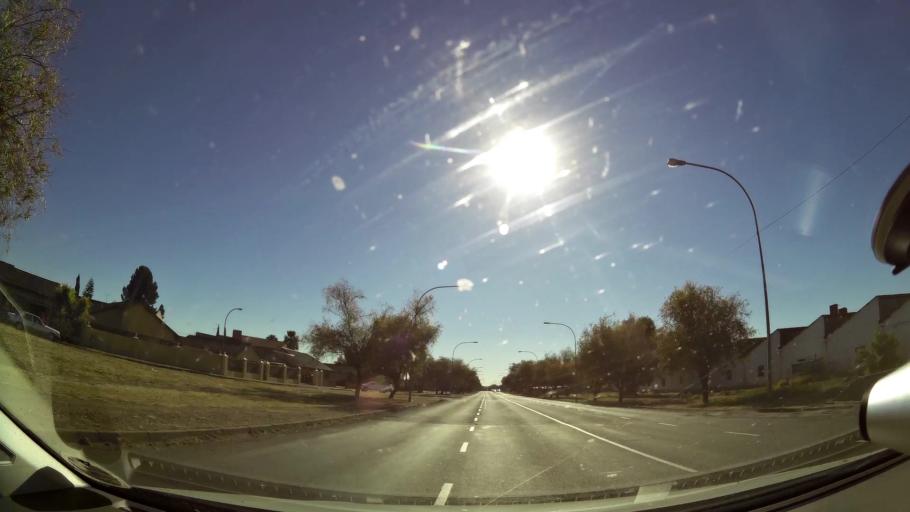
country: ZA
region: Northern Cape
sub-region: Frances Baard District Municipality
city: Kimberley
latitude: -28.7227
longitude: 24.7712
